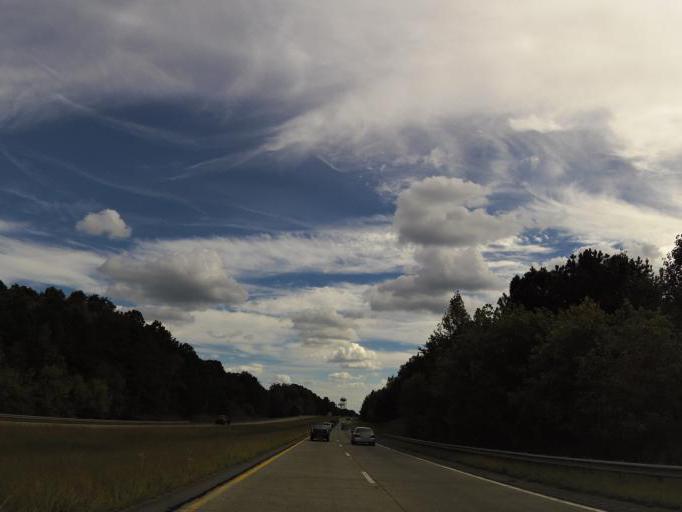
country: US
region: Georgia
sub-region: Pickens County
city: Jasper
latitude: 34.4368
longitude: -84.4372
